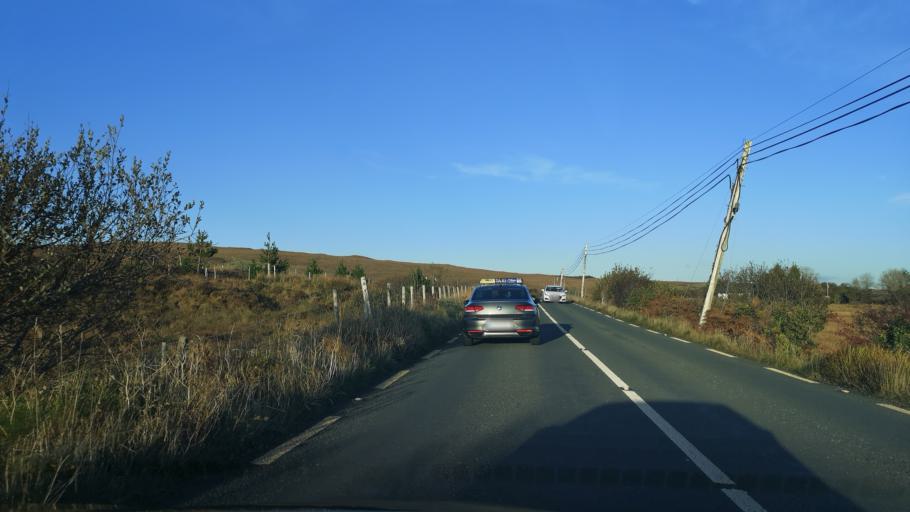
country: IE
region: Connaught
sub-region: County Galway
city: Oughterard
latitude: 53.4214
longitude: -9.3833
